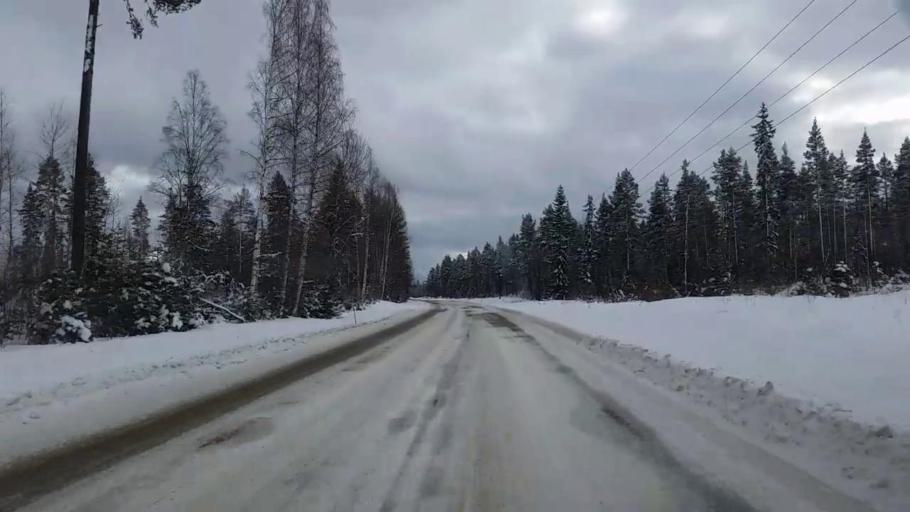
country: SE
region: Jaemtland
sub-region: Harjedalens Kommun
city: Sveg
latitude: 62.1027
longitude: 15.0695
